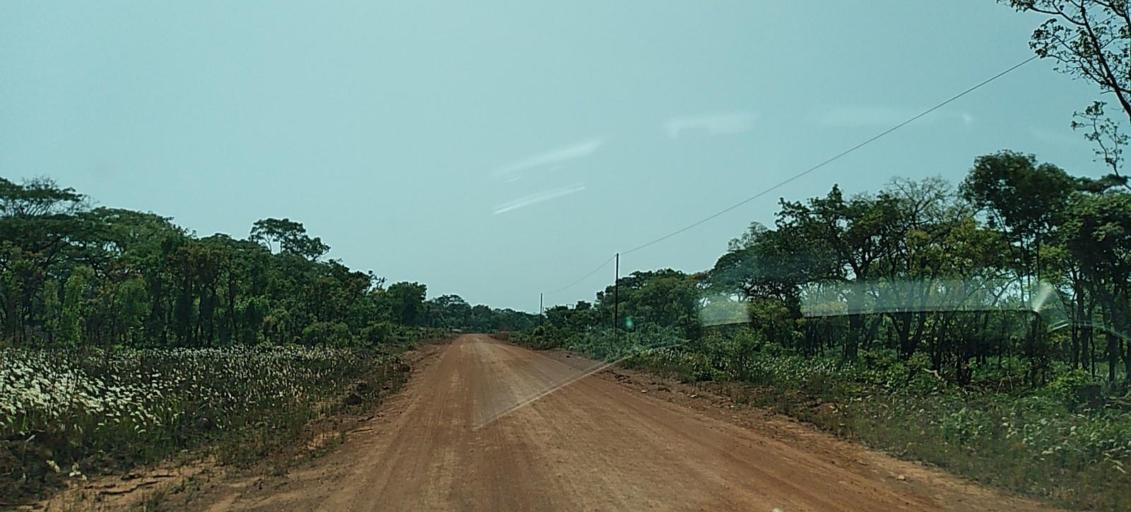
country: ZM
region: North-Western
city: Kansanshi
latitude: -11.9941
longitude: 26.6438
